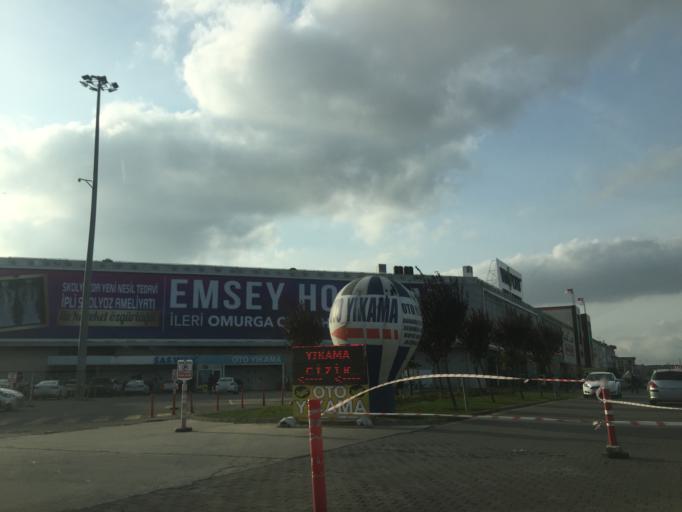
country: TR
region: Istanbul
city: Sultanbeyli
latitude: 40.9371
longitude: 29.3279
